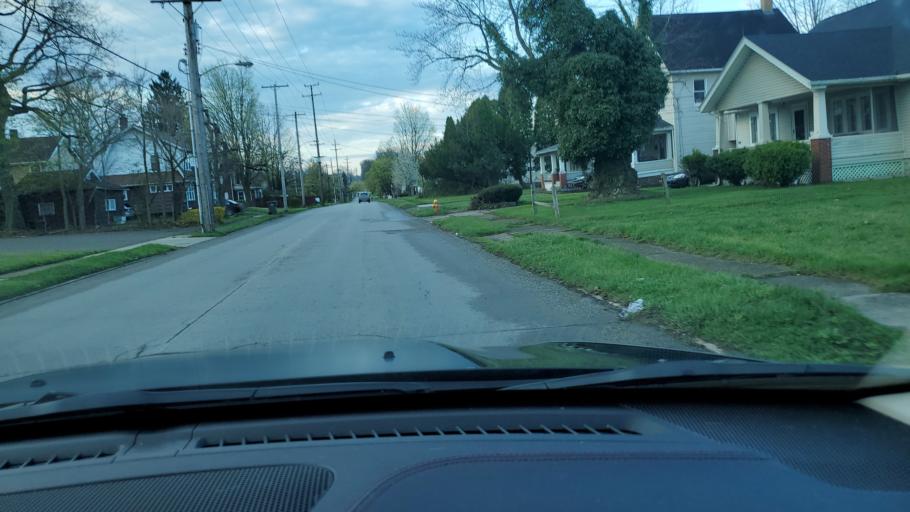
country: US
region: Ohio
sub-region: Mahoning County
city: Youngstown
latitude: 41.0710
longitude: -80.6640
